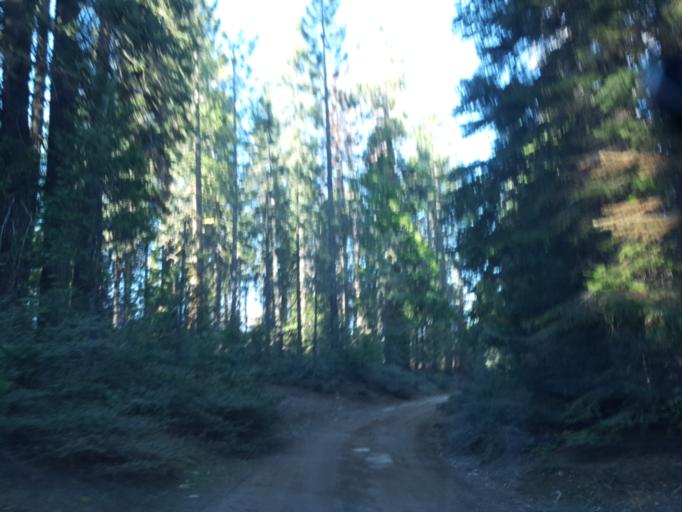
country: US
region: California
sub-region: Madera County
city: Oakhurst
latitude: 37.3637
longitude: -119.4771
